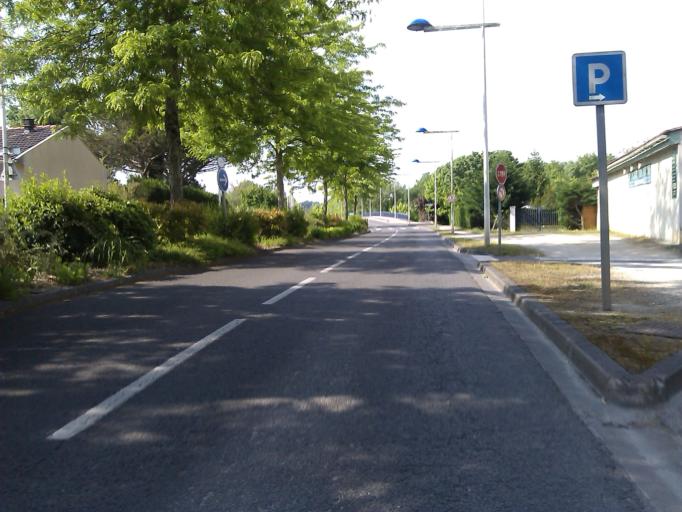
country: FR
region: Poitou-Charentes
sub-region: Departement de la Charente
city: Angouleme
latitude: 45.6584
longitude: 0.1419
